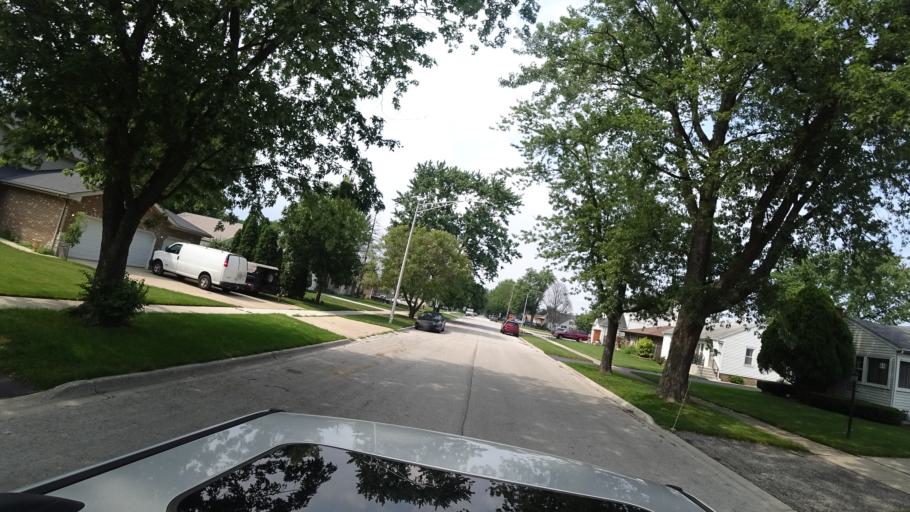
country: US
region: Illinois
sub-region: Cook County
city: Chicago Ridge
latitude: 41.6969
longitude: -87.7765
